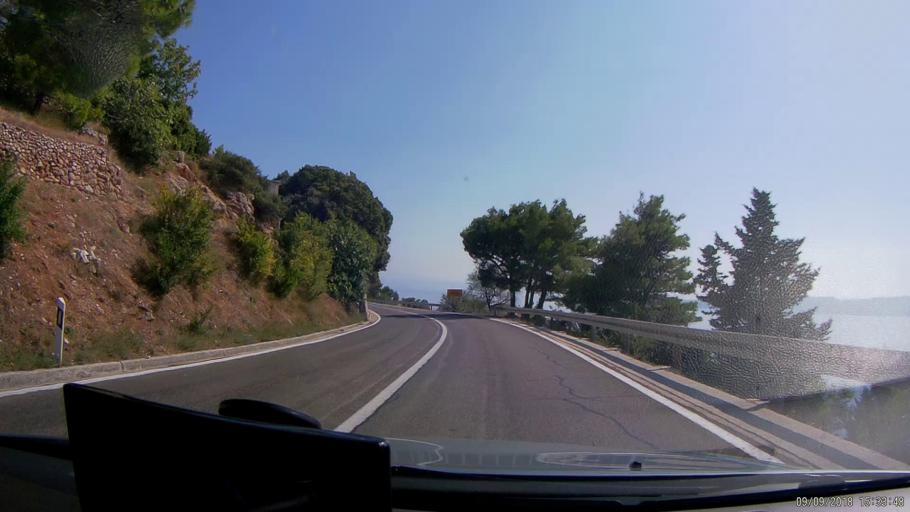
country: HR
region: Splitsko-Dalmatinska
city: Donja Brela
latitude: 43.3912
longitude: 16.9001
